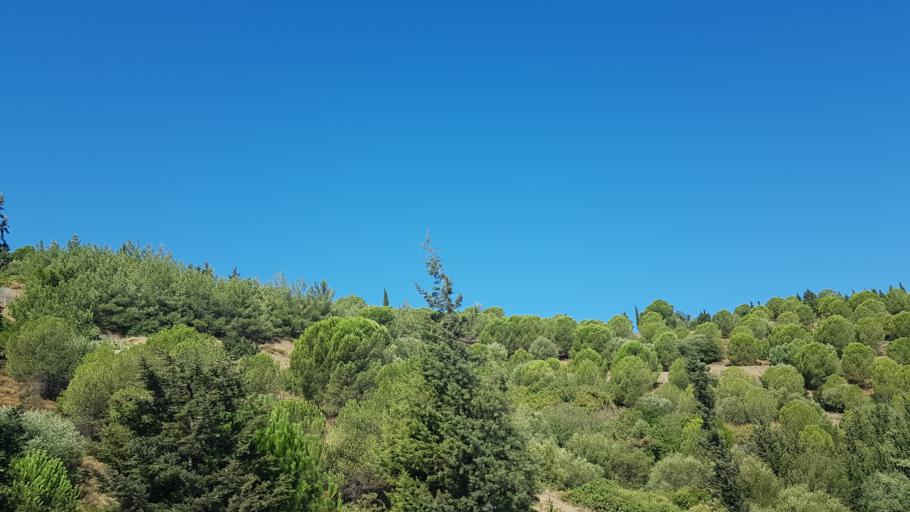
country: TR
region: Izmir
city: Buca
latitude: 38.3991
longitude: 27.2293
